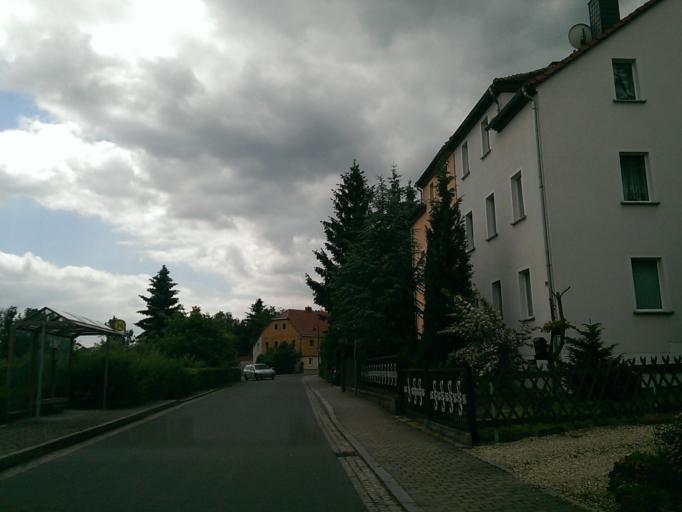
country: DE
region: Saxony
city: Bertsdorf-Hoernitz
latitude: 50.8952
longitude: 14.7496
